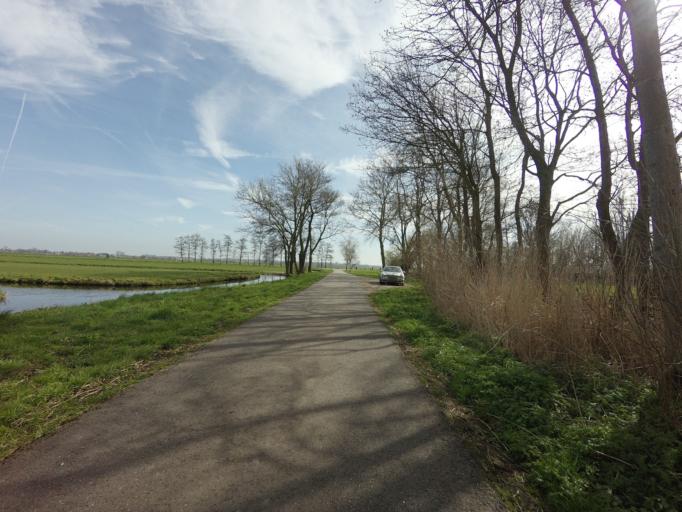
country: NL
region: South Holland
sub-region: Bodegraven-Reeuwijk
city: Bodegraven
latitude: 52.0822
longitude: 4.7143
